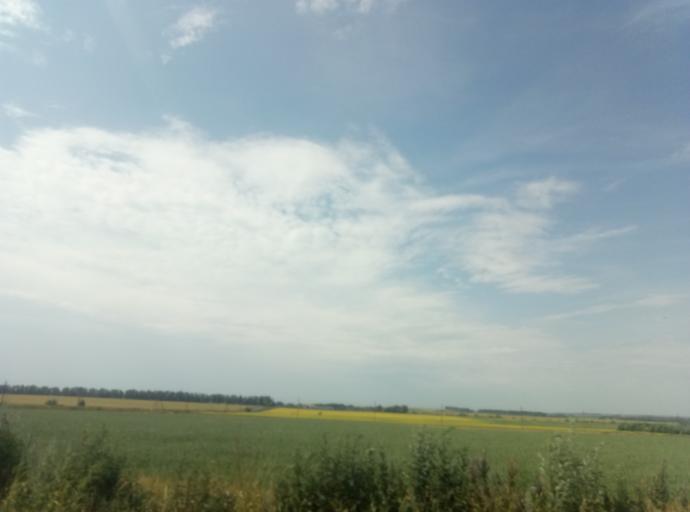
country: RU
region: Tula
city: Dubovka
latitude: 53.8939
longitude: 38.0449
